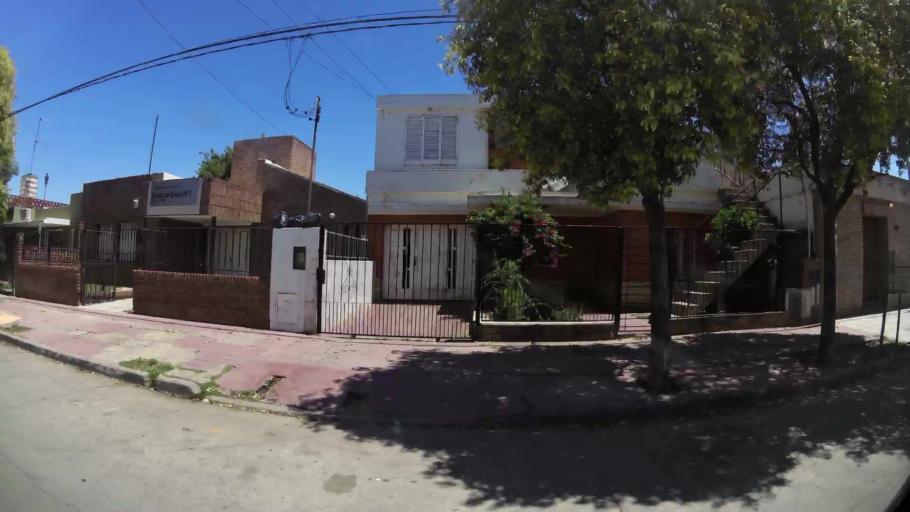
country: AR
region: Cordoba
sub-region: Departamento de Capital
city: Cordoba
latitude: -31.3867
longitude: -64.1304
